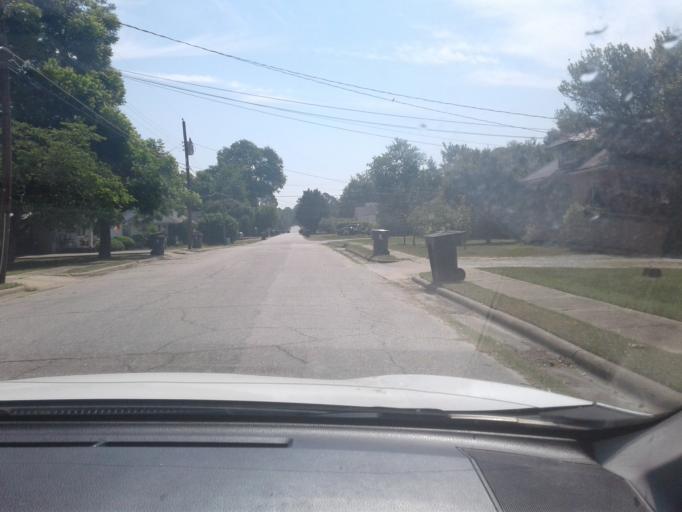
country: US
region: North Carolina
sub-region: Harnett County
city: Erwin
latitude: 35.3238
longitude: -78.6801
